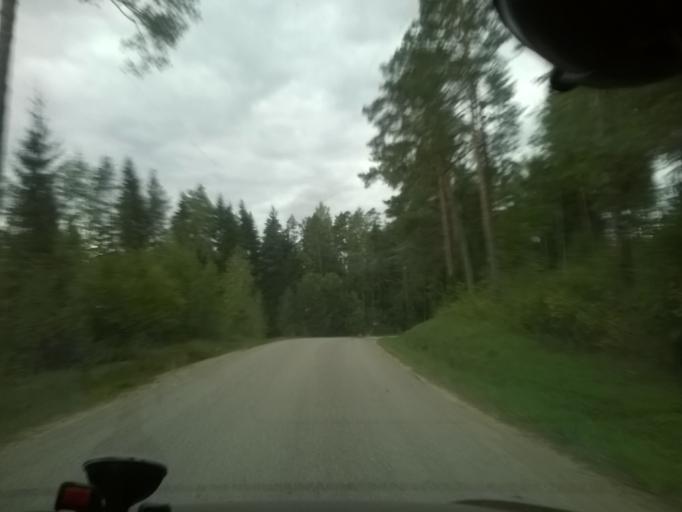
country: EE
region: Vorumaa
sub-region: Voru linn
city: Voru
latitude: 57.8172
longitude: 27.1159
